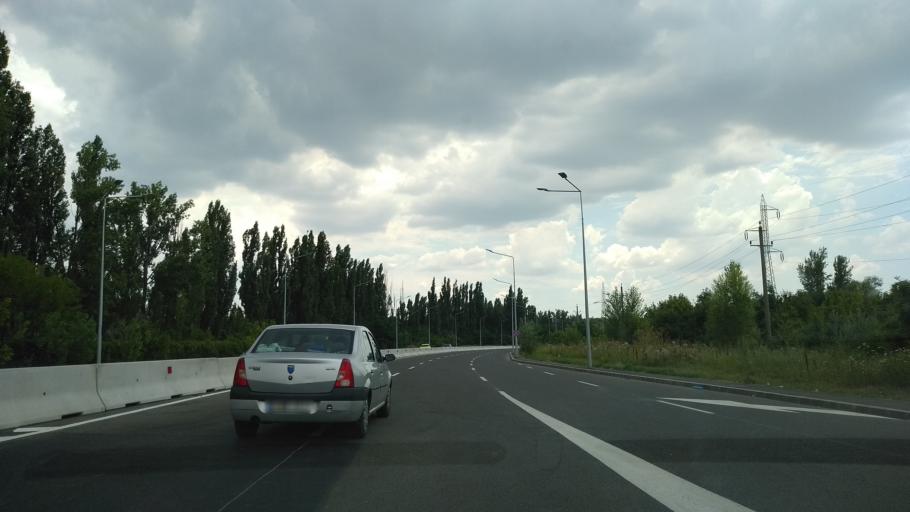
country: RO
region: Ilfov
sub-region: Comuna Popesti-Leordeni
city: Popesti-Leordeni
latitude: 44.3961
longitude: 26.1580
